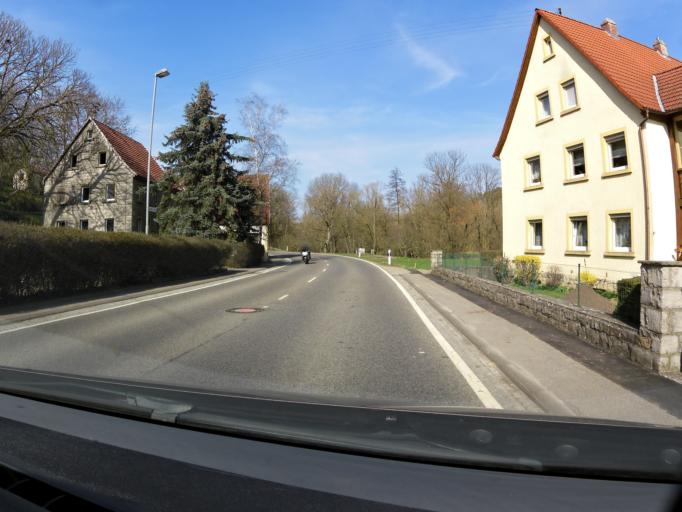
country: DE
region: Baden-Wuerttemberg
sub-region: Regierungsbezirk Stuttgart
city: Creglingen
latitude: 49.4929
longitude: 10.0173
